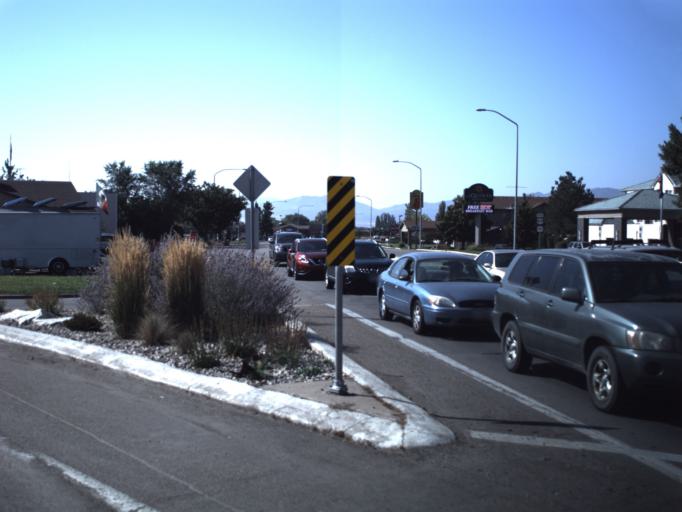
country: US
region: Utah
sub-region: Cache County
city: River Heights
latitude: 41.7172
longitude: -111.8353
